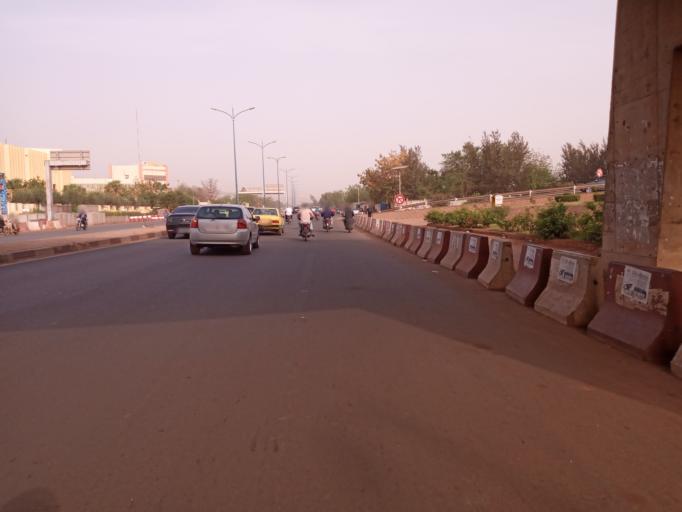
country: ML
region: Bamako
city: Bamako
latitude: 12.6325
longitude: -8.0117
